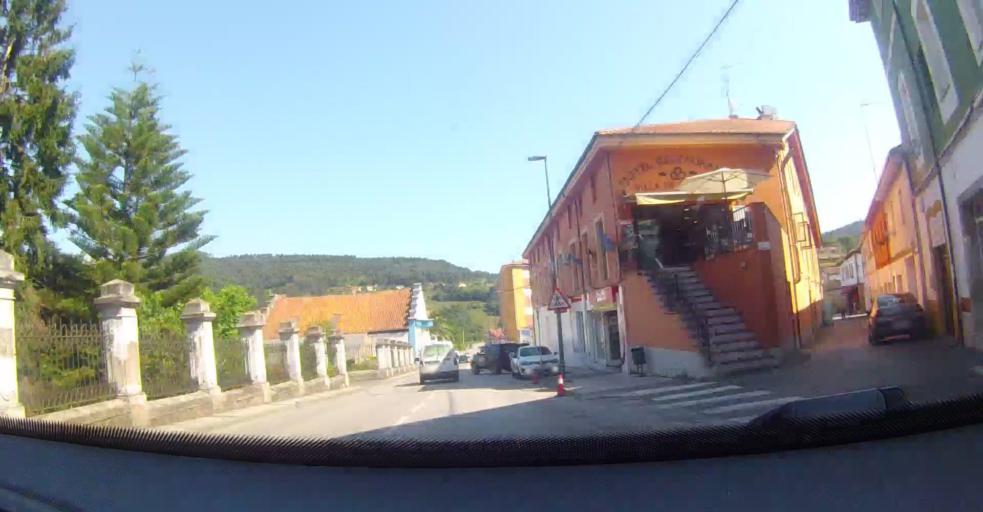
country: ES
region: Asturias
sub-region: Province of Asturias
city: Colunga
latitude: 43.4862
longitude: -5.2700
